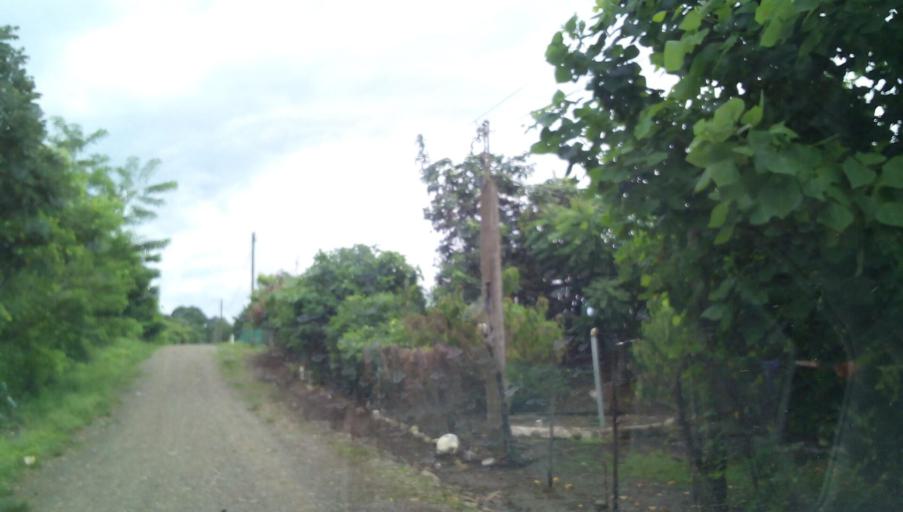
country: MX
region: Veracruz
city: Tepetzintla
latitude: 21.1273
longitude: -97.8578
